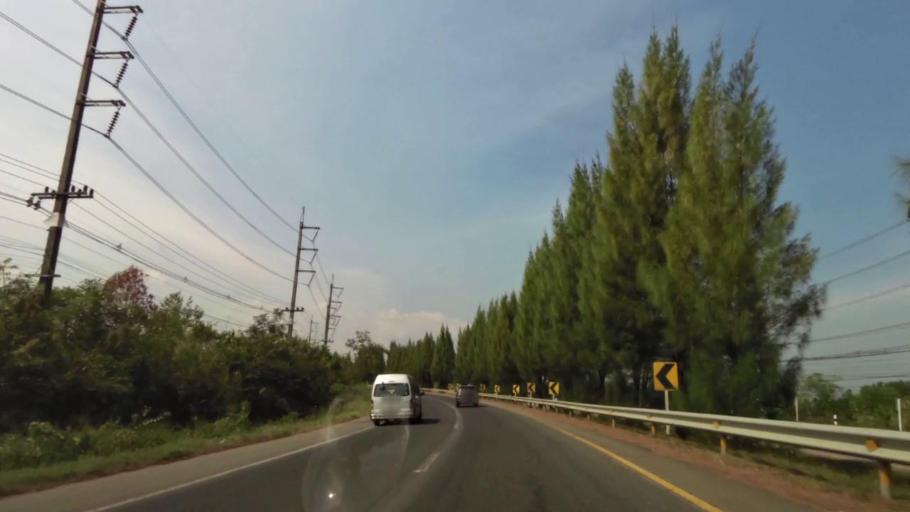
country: TH
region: Chanthaburi
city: Chanthaburi
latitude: 12.6620
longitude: 102.1209
